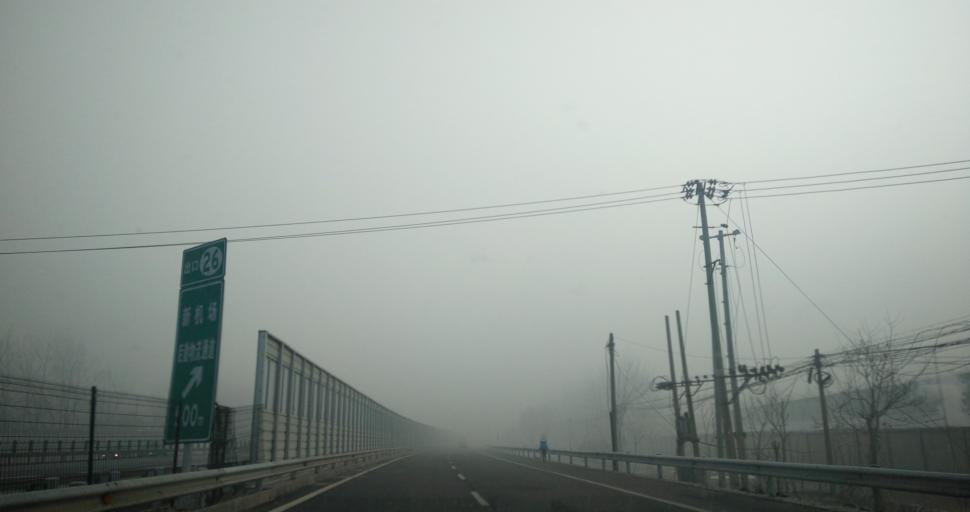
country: CN
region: Beijing
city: Yinghai
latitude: 39.7236
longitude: 116.4453
